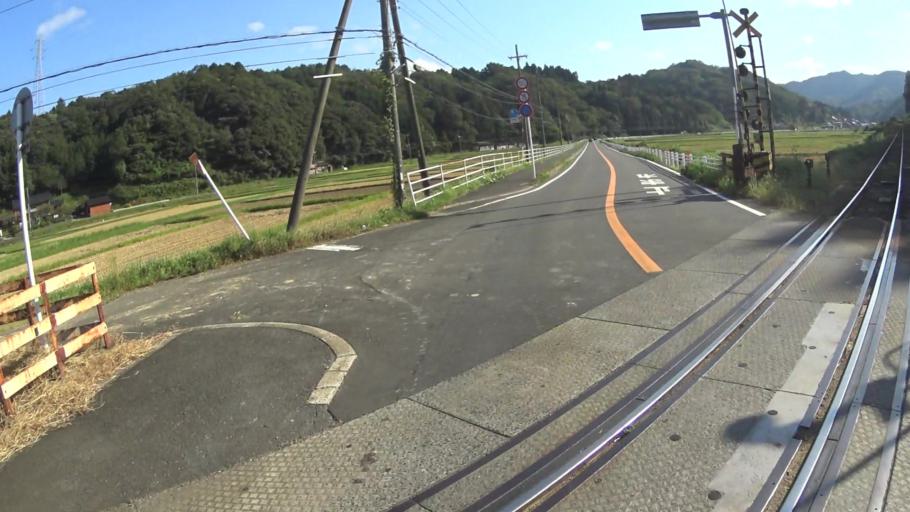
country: JP
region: Kyoto
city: Miyazu
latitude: 35.6661
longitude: 135.0236
